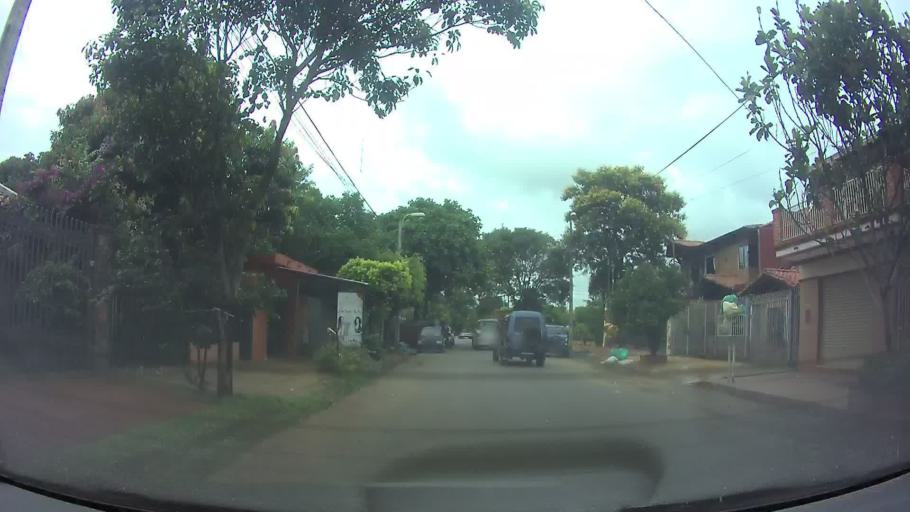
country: PY
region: Central
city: San Lorenzo
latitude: -25.2703
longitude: -57.4834
